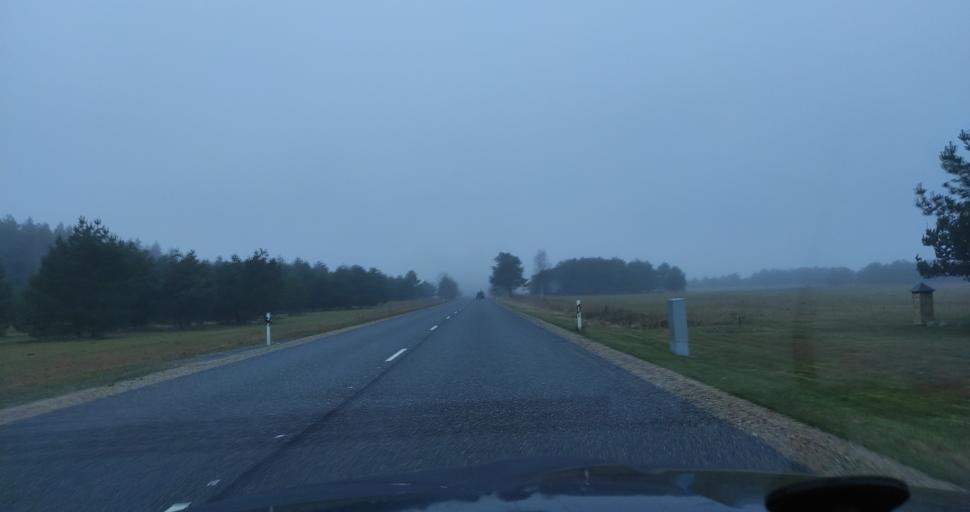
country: LV
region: Pavilostas
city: Pavilosta
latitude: 56.9569
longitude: 21.3215
